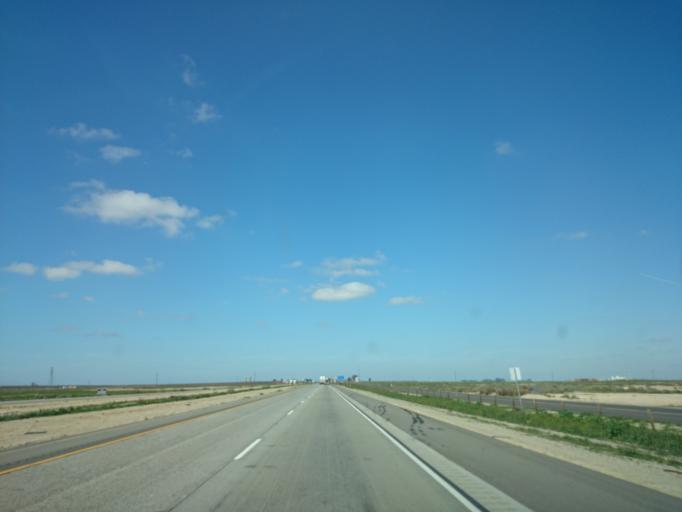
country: US
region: California
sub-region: Kern County
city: Buttonwillow
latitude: 35.4036
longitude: -119.4036
